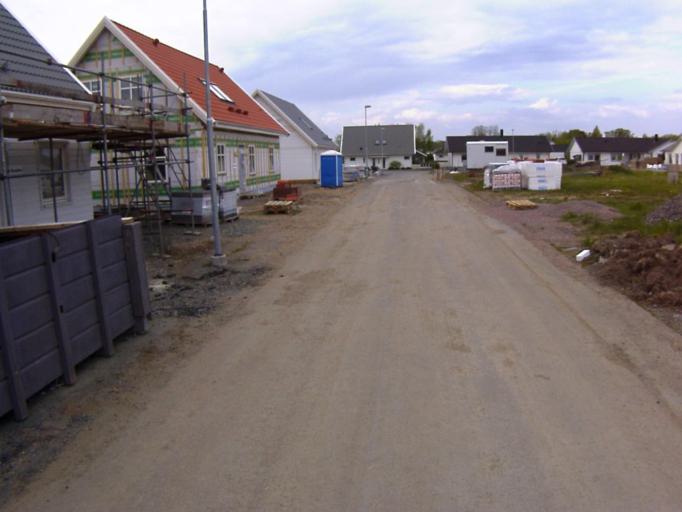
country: SE
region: Skane
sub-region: Kristianstads Kommun
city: Kristianstad
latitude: 56.0161
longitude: 14.1958
